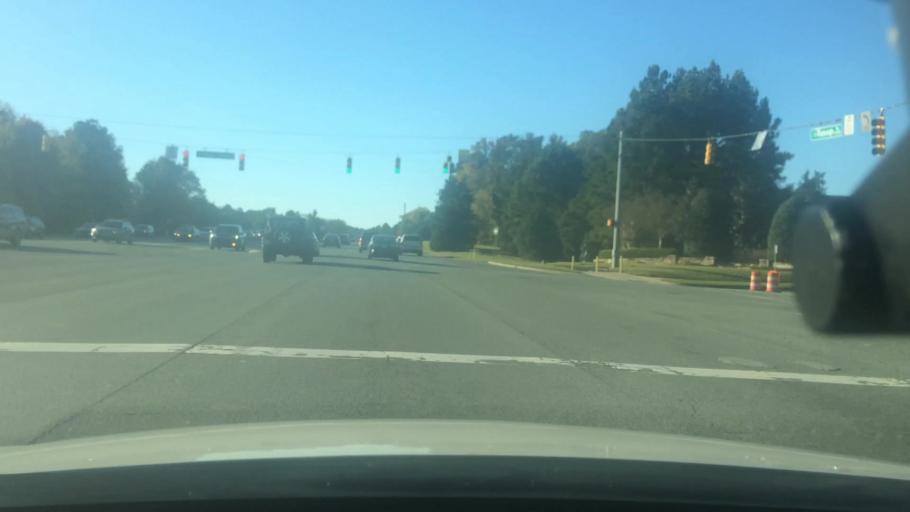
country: US
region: North Carolina
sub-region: Orange County
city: Chapel Hill
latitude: 35.9027
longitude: -79.0102
